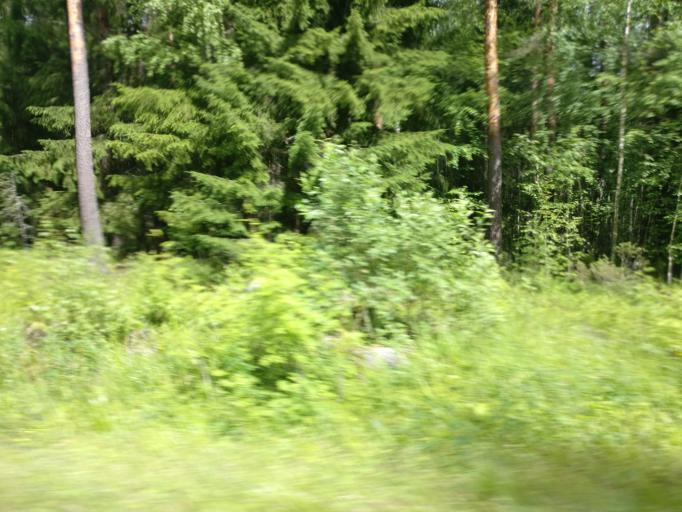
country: FI
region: Southern Savonia
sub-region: Pieksaemaeki
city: Joroinen
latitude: 62.1994
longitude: 27.9893
